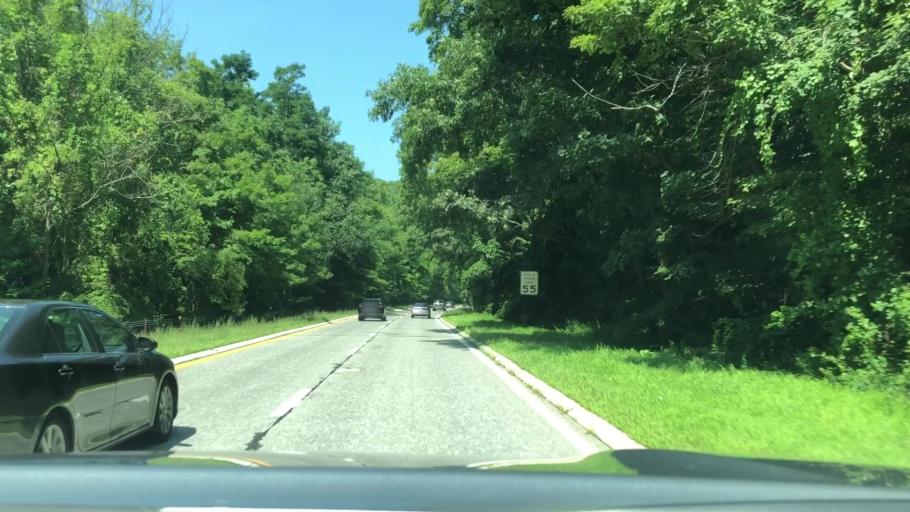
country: US
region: New York
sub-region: Rockland County
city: Thiells
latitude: 41.2500
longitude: -74.0398
